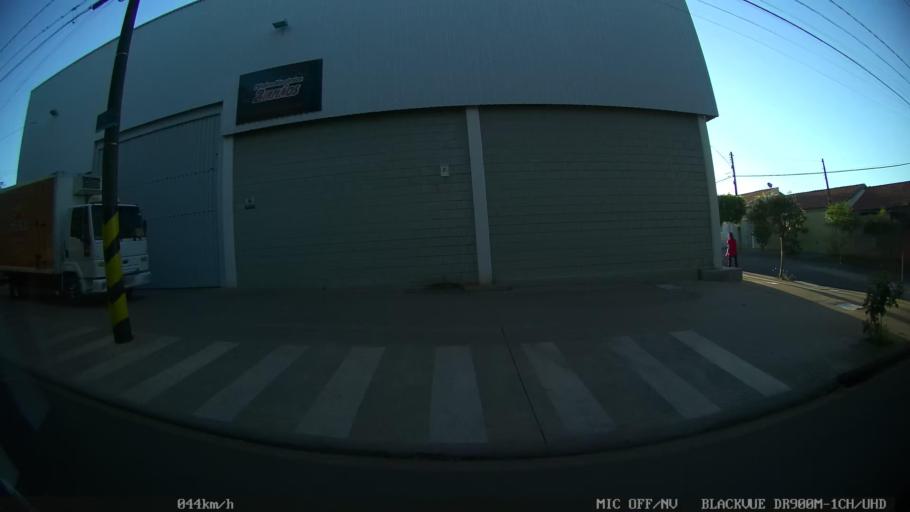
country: BR
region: Sao Paulo
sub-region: Sao Jose Do Rio Preto
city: Sao Jose do Rio Preto
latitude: -20.7752
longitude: -49.3555
